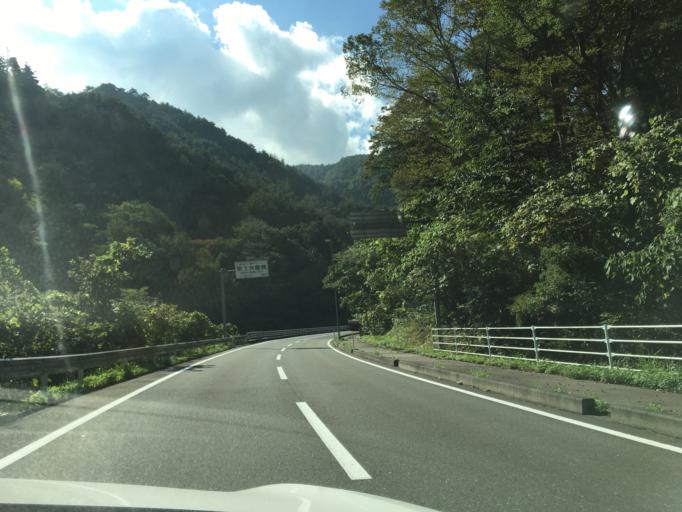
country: JP
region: Fukushima
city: Namie
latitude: 37.5083
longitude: 140.9029
